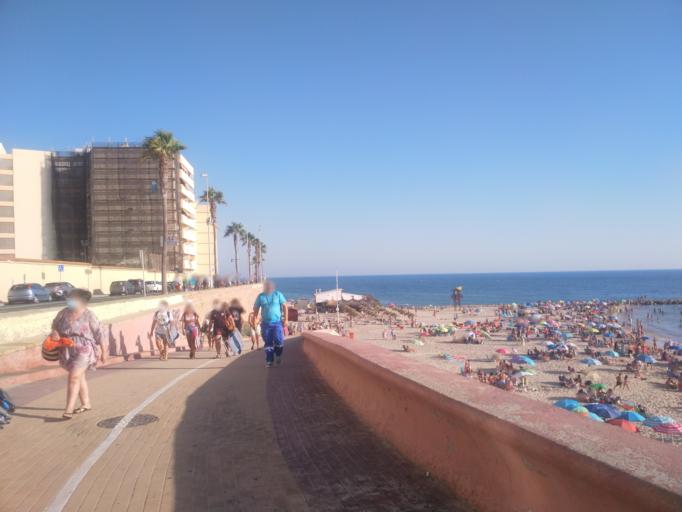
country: ES
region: Andalusia
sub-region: Provincia de Cadiz
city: Cadiz
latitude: 36.5190
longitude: -6.2862
